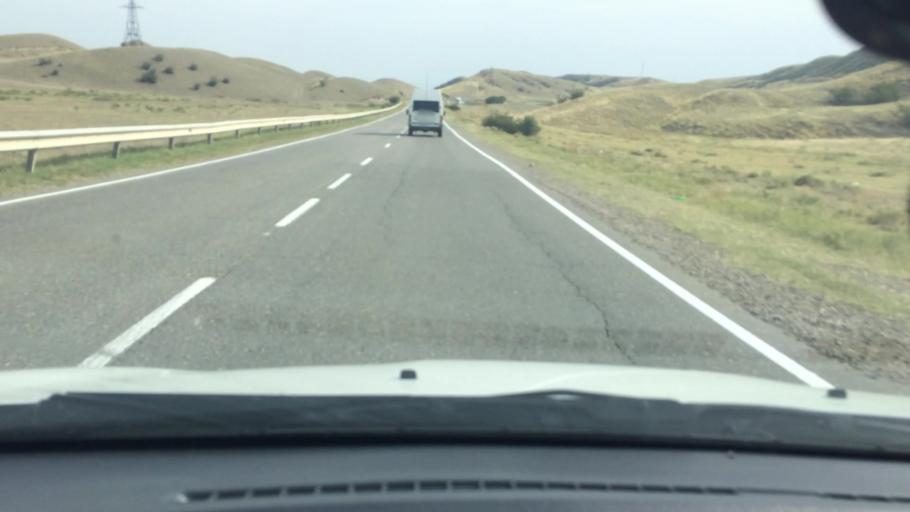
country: GE
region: Kvemo Kartli
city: Rust'avi
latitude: 41.5341
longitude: 44.9810
